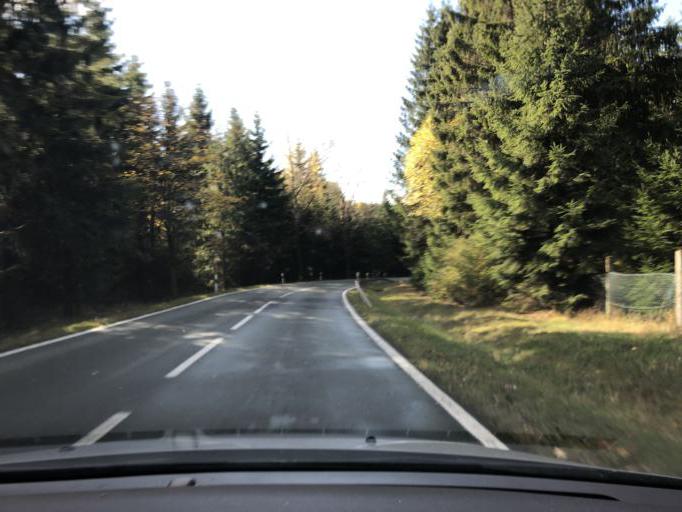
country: DE
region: Thuringia
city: Neuhaus am Rennweg
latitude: 50.5207
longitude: 11.1371
